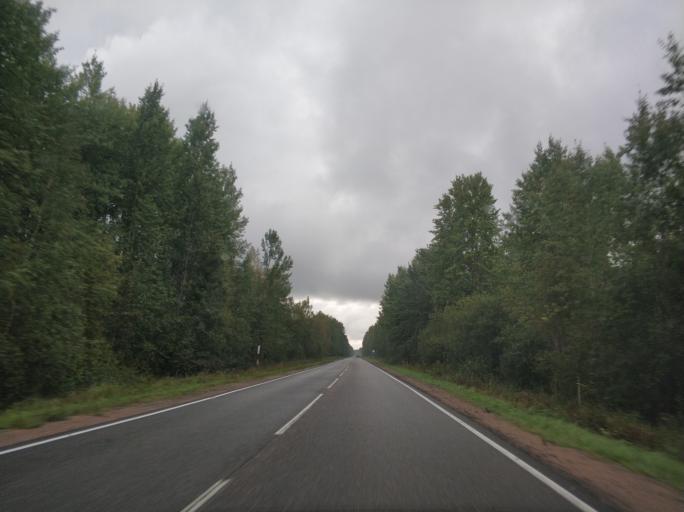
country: RU
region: Leningrad
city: Borisova Griva
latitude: 60.1159
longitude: 30.9638
